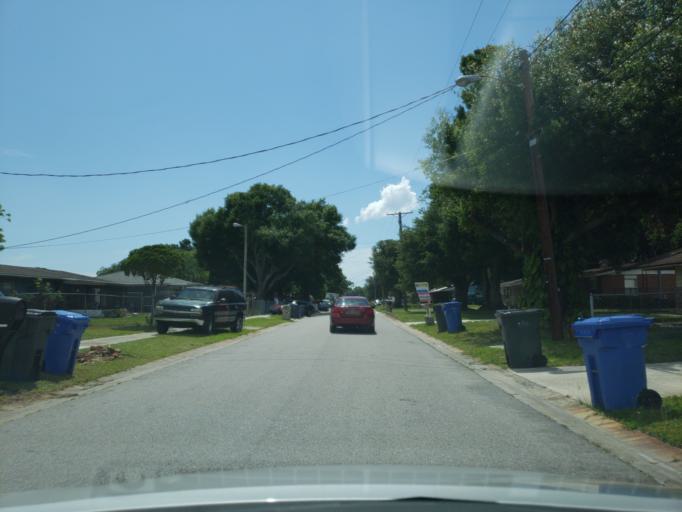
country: US
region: Florida
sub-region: Hillsborough County
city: Progress Village
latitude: 27.8987
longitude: -82.3617
